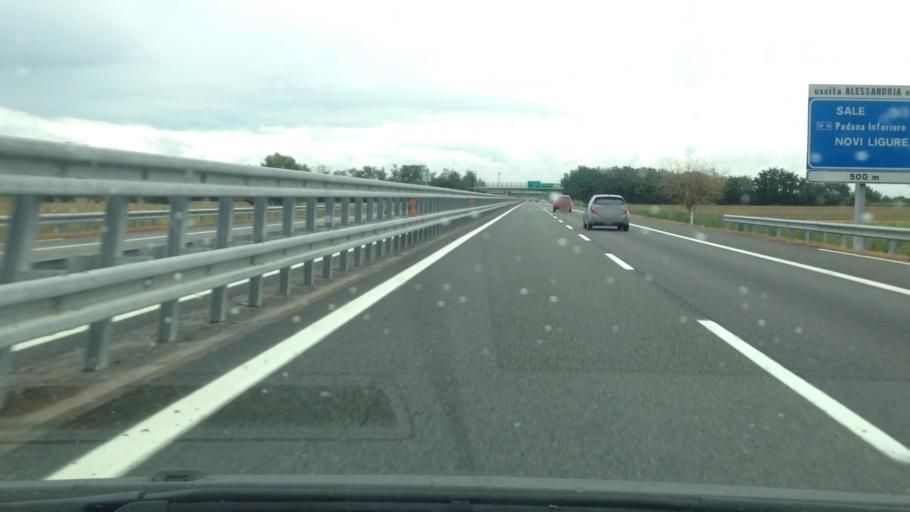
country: IT
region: Piedmont
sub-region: Provincia di Alessandria
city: Castelceriolo
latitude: 44.9253
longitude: 8.6914
